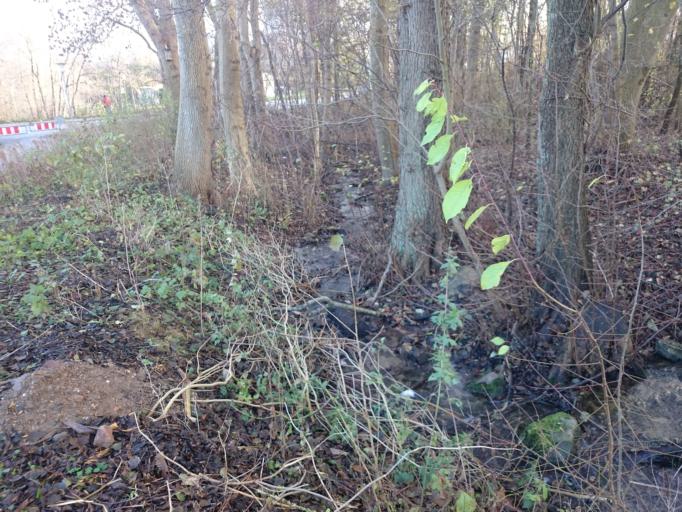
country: DK
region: Central Jutland
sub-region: Arhus Kommune
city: Stavtrup
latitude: 56.1233
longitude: 10.1316
